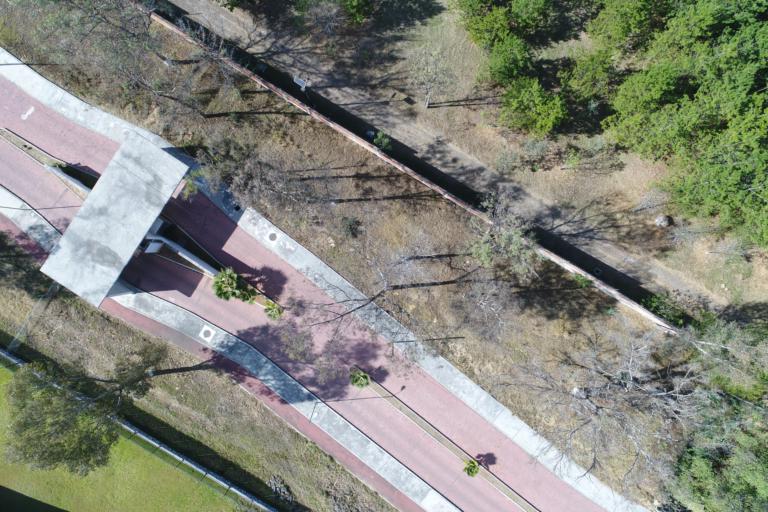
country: MX
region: Michoacan
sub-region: Morelia
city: Morelos
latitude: 19.6501
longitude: -101.2299
